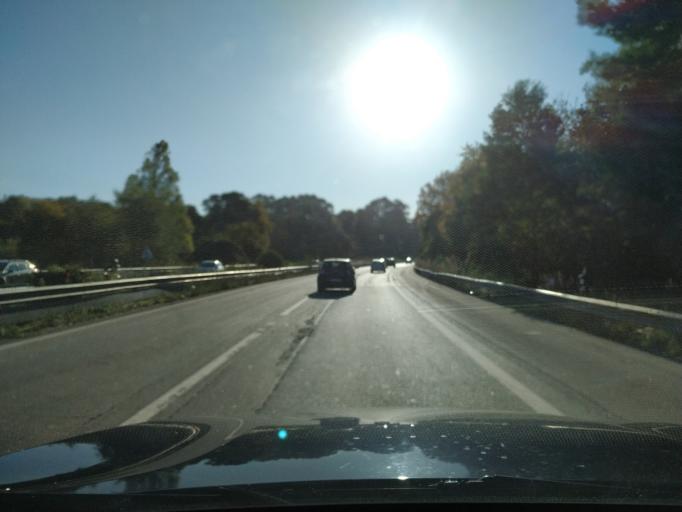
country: PT
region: Porto
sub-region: Vila Nova de Gaia
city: Vilar de Andorinho
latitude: 41.1108
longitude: -8.6085
